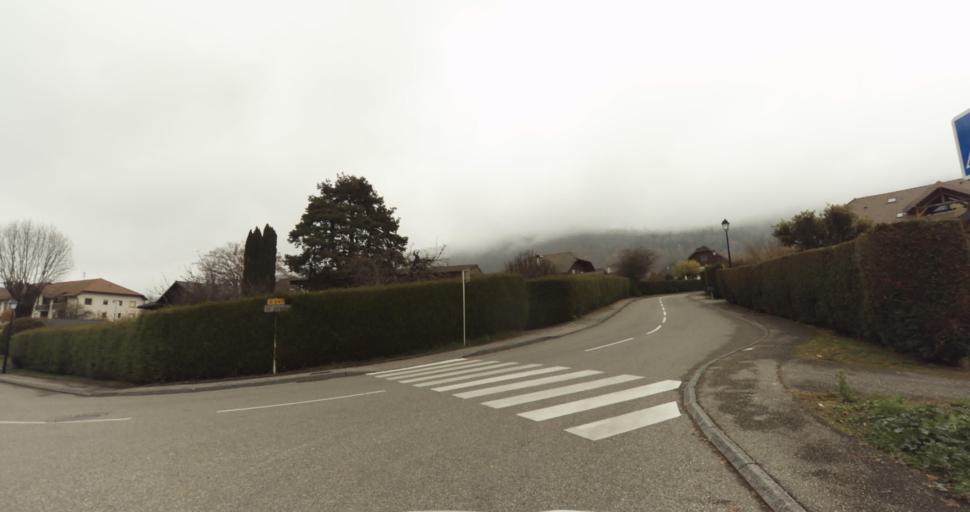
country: FR
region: Rhone-Alpes
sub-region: Departement de la Haute-Savoie
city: Viuz-la-Chiesaz
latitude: 45.8387
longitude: 6.0829
